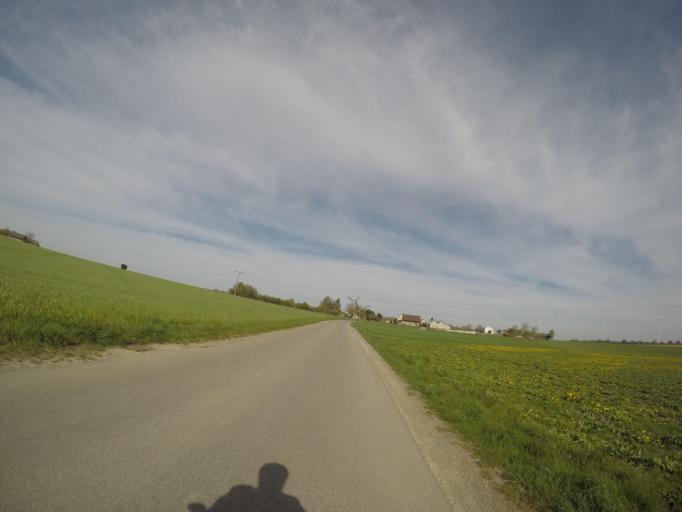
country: DE
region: Baden-Wuerttemberg
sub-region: Tuebingen Region
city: Allmannsweiler
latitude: 48.0009
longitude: 9.5796
